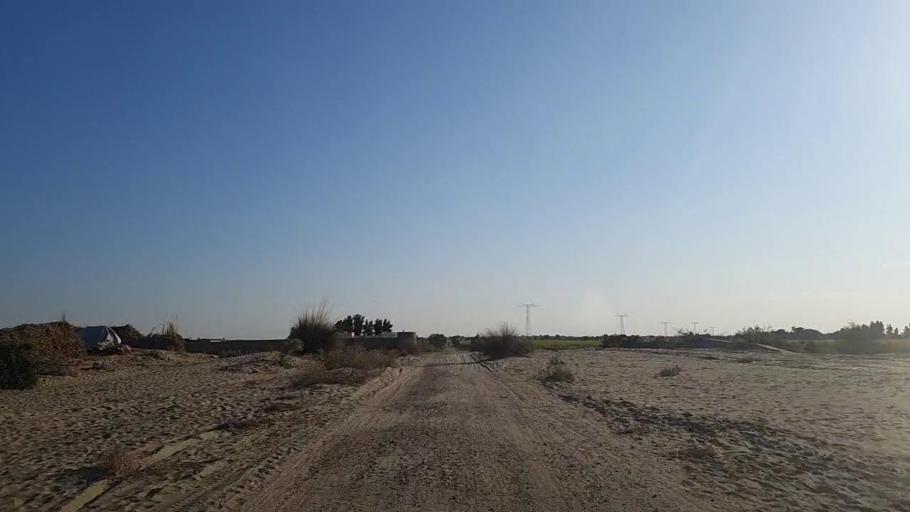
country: PK
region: Sindh
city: Khadro
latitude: 26.2714
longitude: 68.8604
